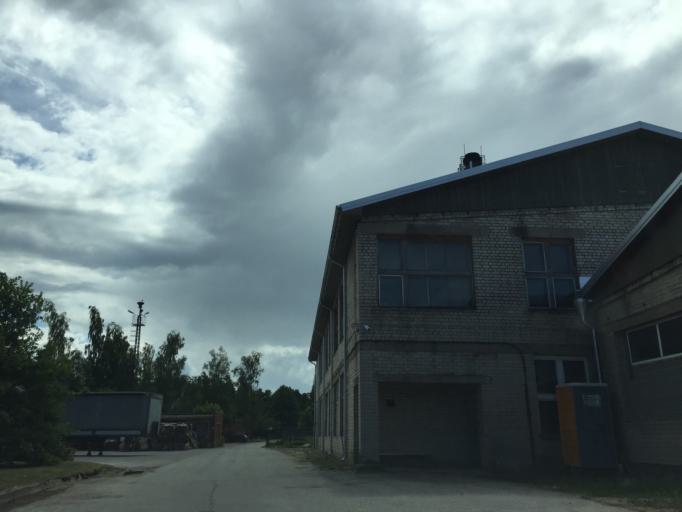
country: LV
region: Saulkrastu
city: Saulkrasti
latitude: 57.3161
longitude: 24.4128
